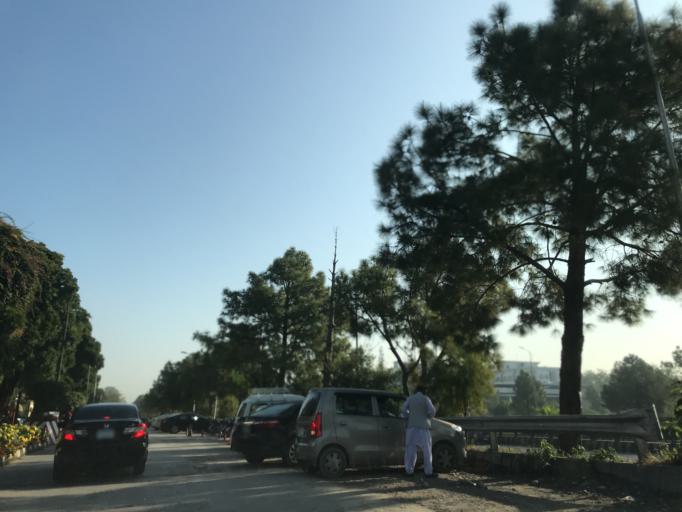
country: PK
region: Islamabad
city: Islamabad
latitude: 33.7141
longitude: 73.0632
